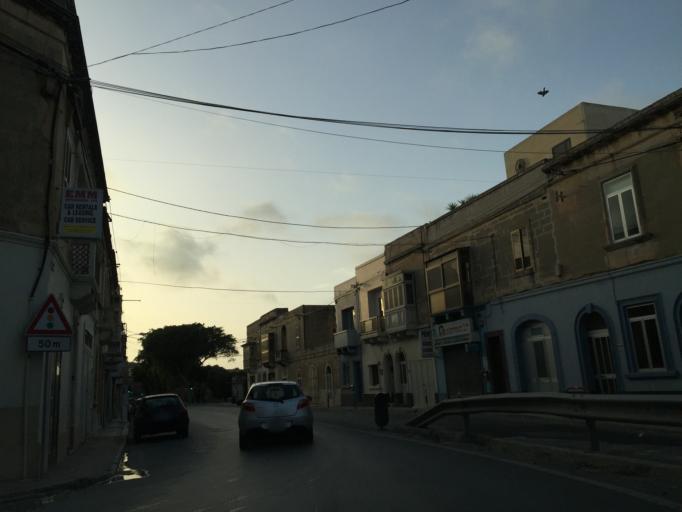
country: MT
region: Saint Paul's Bay
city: San Pawl il-Bahar
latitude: 35.9359
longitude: 14.4139
